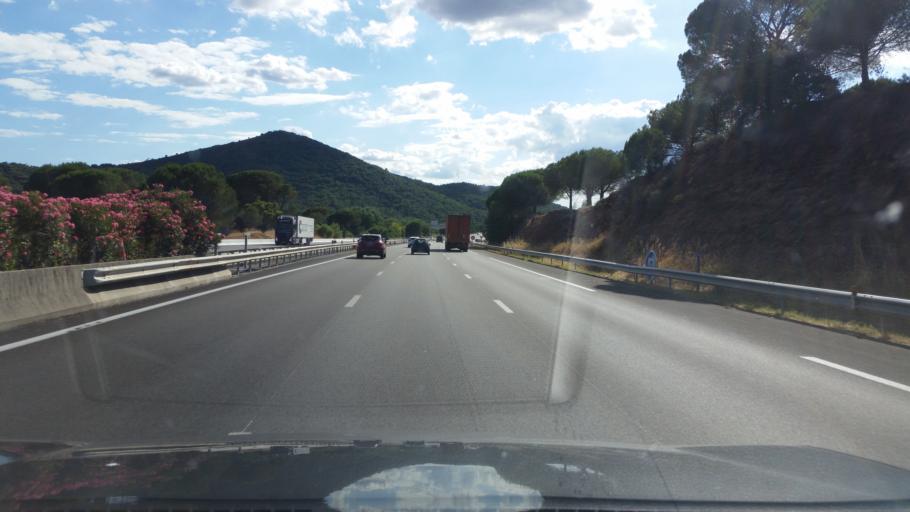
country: FR
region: Provence-Alpes-Cote d'Azur
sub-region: Departement du Var
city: Le Muy
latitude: 43.4586
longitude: 6.5524
